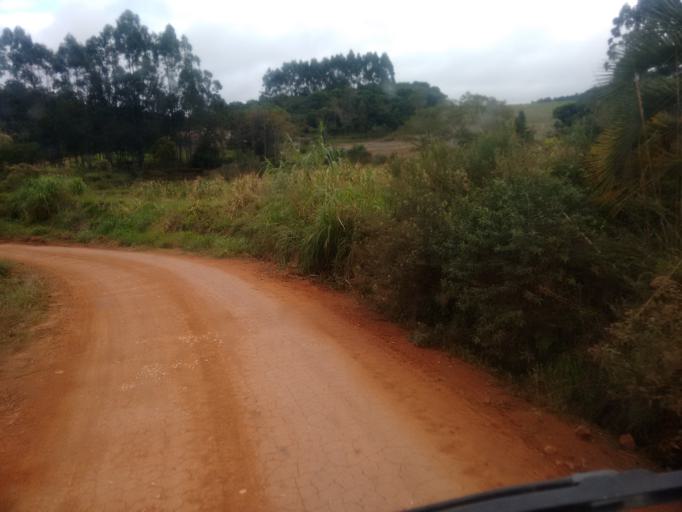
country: BR
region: Rio Grande do Sul
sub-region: Camaqua
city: Camaqua
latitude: -30.7219
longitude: -51.8684
